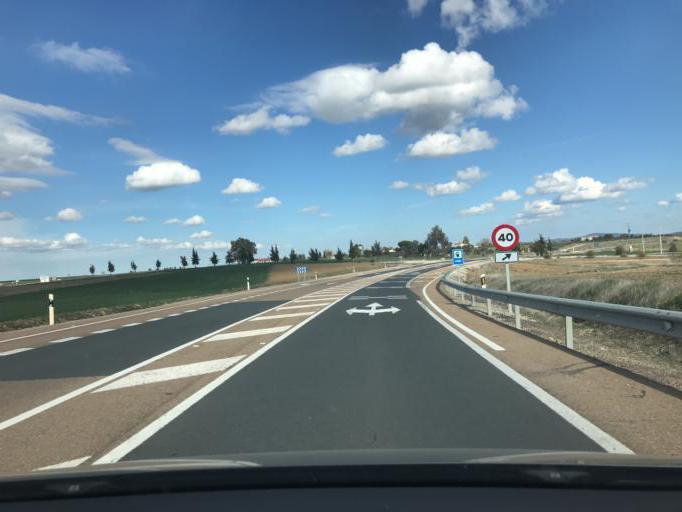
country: ES
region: Extremadura
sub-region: Provincia de Badajoz
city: Azuaga
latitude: 38.2754
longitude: -5.6797
